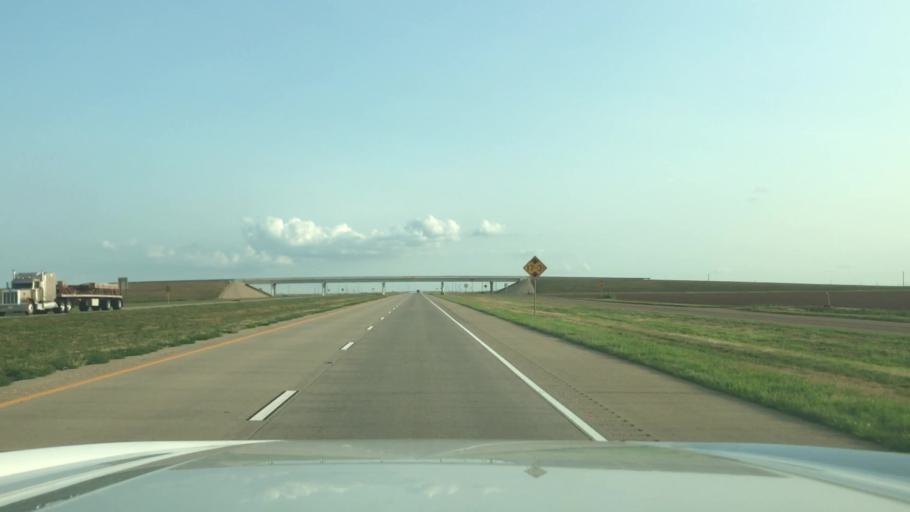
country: US
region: Texas
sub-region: Swisher County
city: Tulia
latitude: 34.4745
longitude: -101.7772
